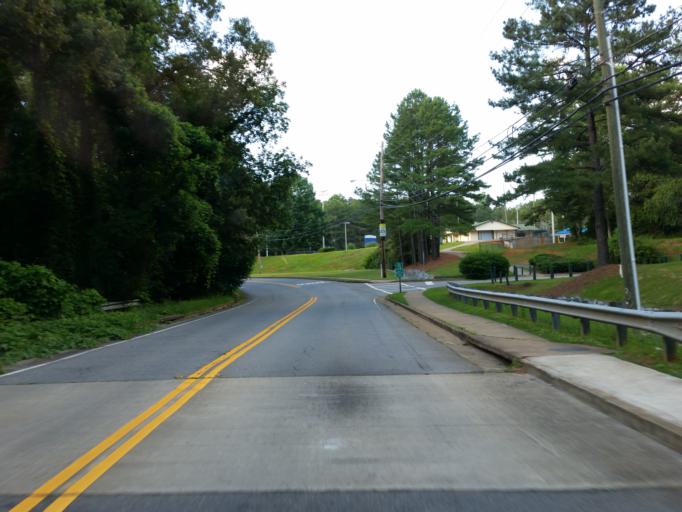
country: US
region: Georgia
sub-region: Cherokee County
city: Woodstock
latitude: 34.0576
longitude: -84.4745
